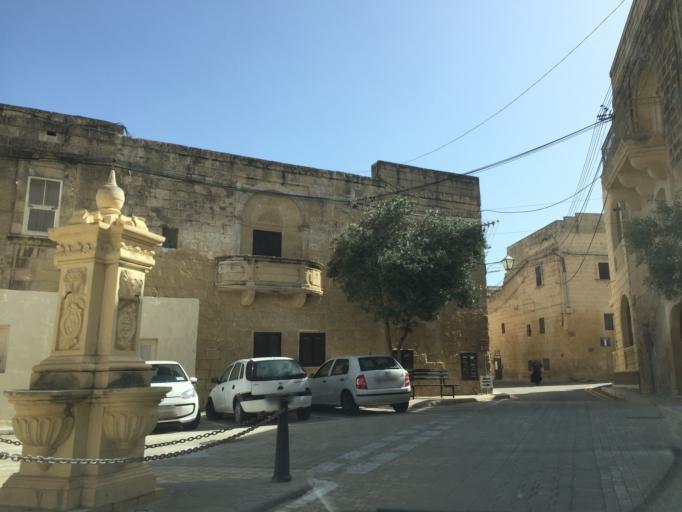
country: MT
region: L-Gharb
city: Gharb
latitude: 36.0624
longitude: 14.2092
